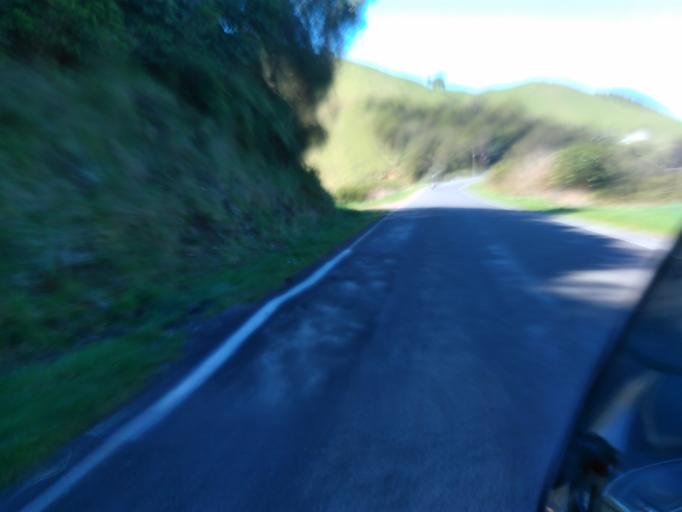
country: NZ
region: Bay of Plenty
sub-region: Opotiki District
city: Opotiki
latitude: -38.3173
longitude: 177.5312
